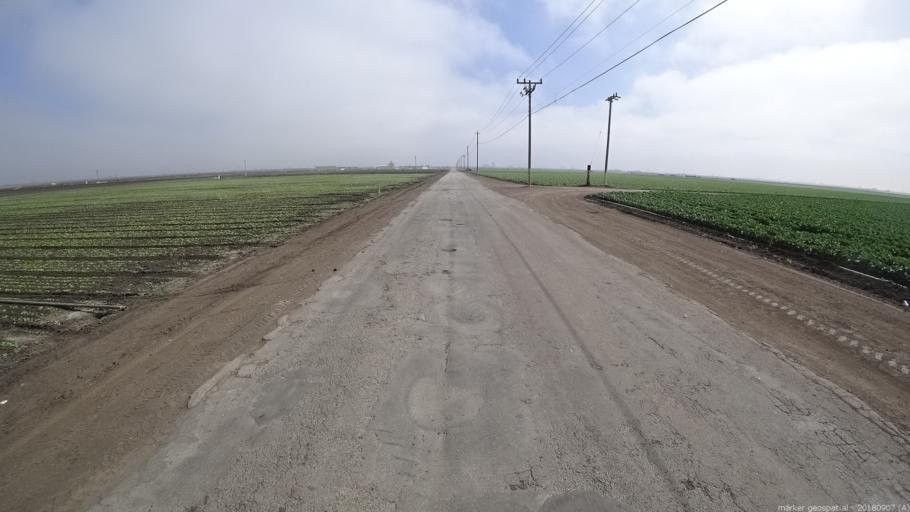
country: US
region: California
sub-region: Monterey County
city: Boronda
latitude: 36.7100
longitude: -121.7263
